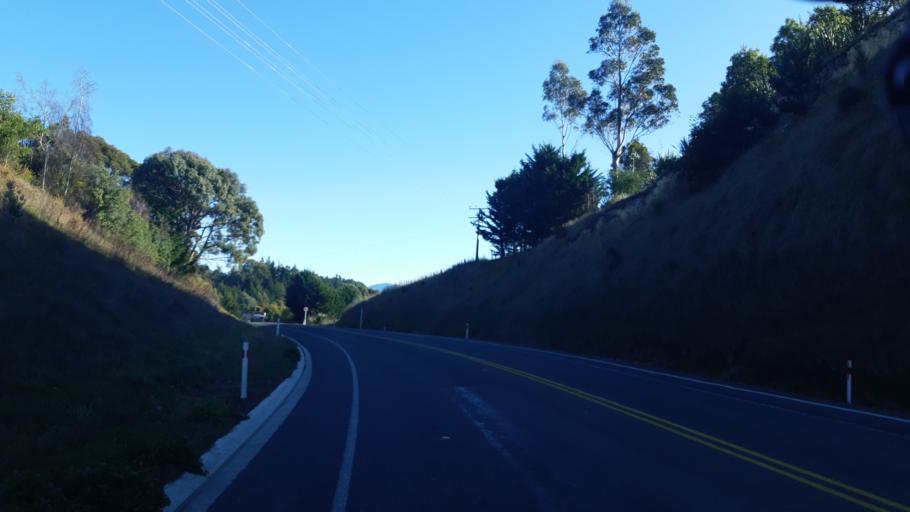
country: NZ
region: Tasman
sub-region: Tasman District
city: Mapua
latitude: -41.2917
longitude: 173.0921
